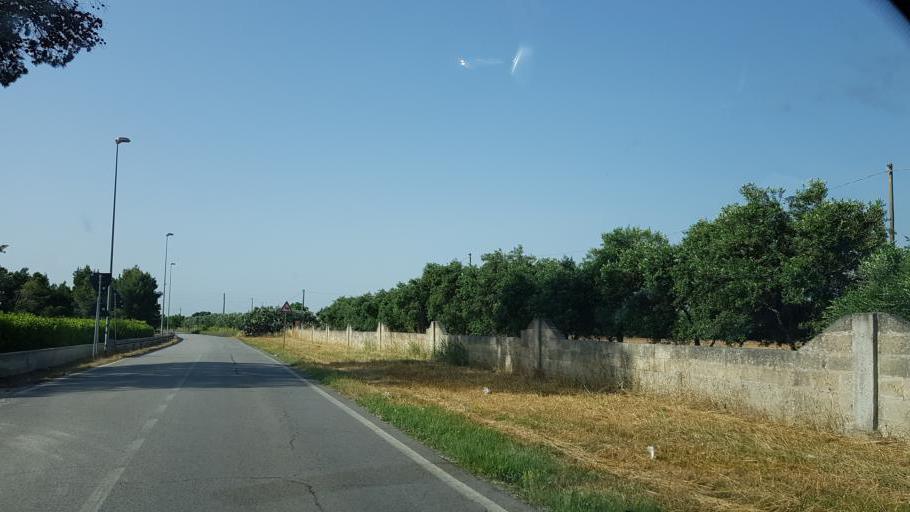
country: IT
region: Apulia
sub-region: Provincia di Brindisi
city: Mesagne
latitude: 40.5409
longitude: 17.8168
